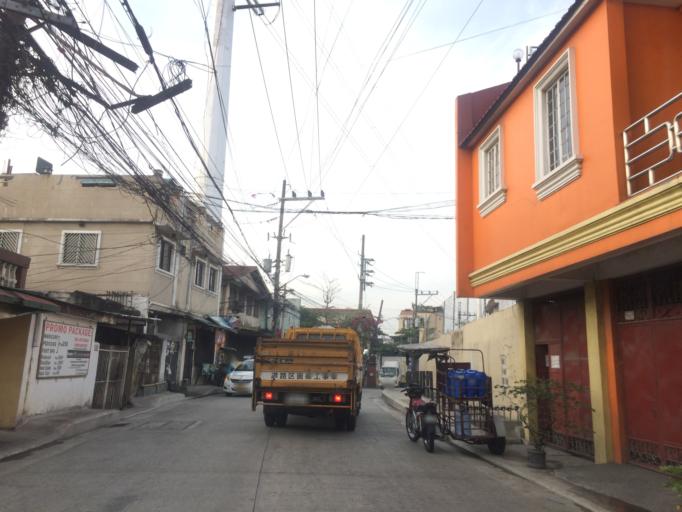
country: PH
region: Calabarzon
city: Del Monte
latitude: 14.6492
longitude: 121.0098
